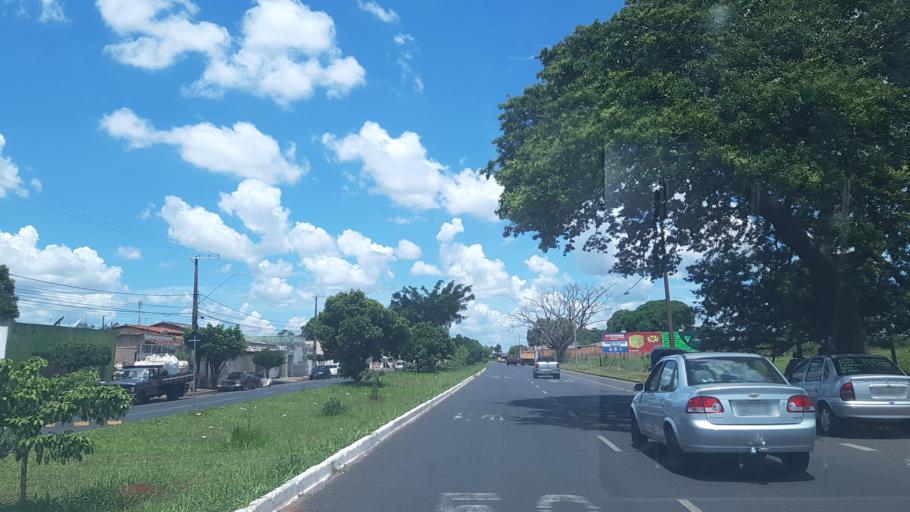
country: BR
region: Minas Gerais
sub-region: Uberlandia
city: Uberlandia
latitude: -18.9496
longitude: -48.3175
